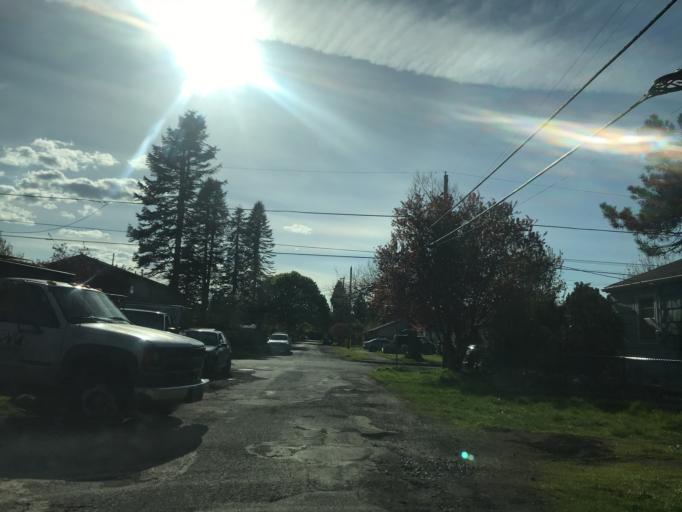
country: US
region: Oregon
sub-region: Multnomah County
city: Lents
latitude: 45.4989
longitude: -122.5961
